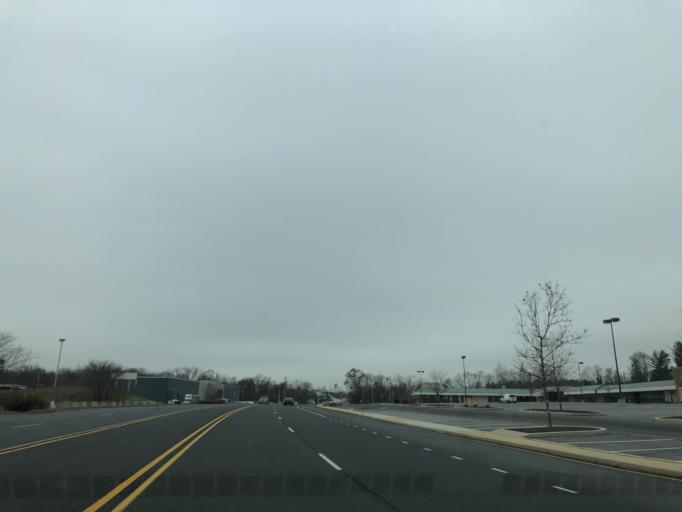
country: US
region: Delaware
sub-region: New Castle County
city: Edgemoor
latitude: 39.7527
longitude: -75.5115
